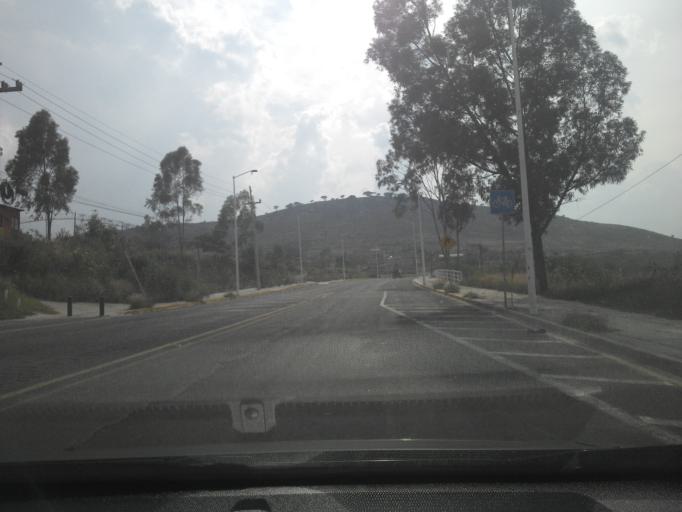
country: MX
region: Jalisco
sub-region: Tlajomulco de Zuniga
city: Lomas del Sur
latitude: 20.4911
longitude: -103.4182
